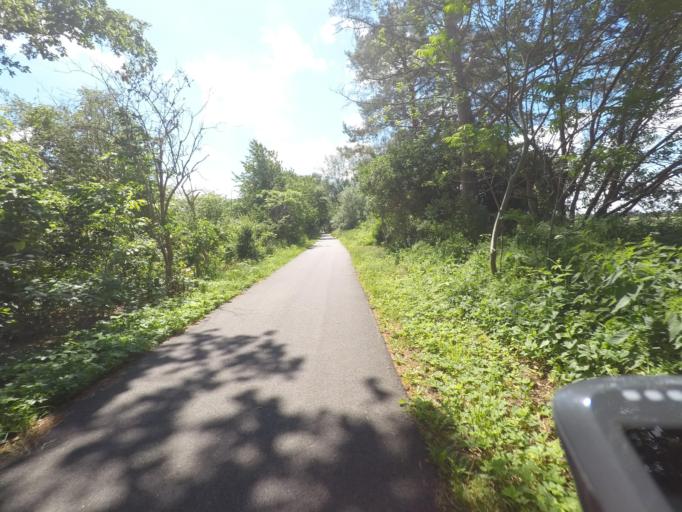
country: DE
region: Hamburg
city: Bergedorf
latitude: 53.4432
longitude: 10.2174
